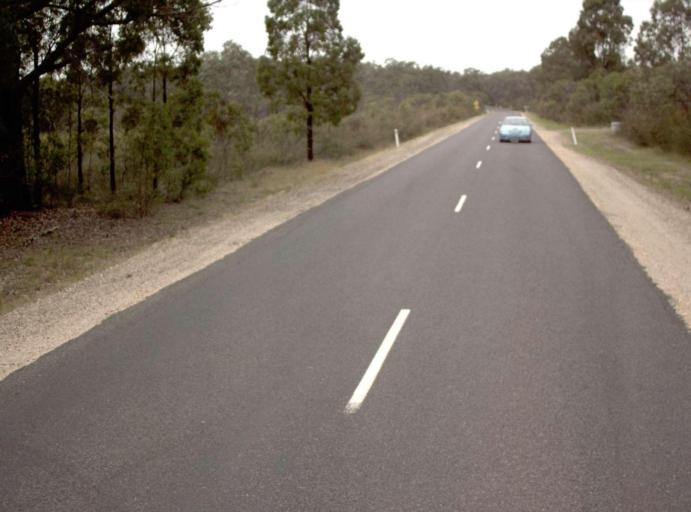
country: AU
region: Victoria
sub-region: Wellington
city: Heyfield
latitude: -37.9258
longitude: 146.7552
